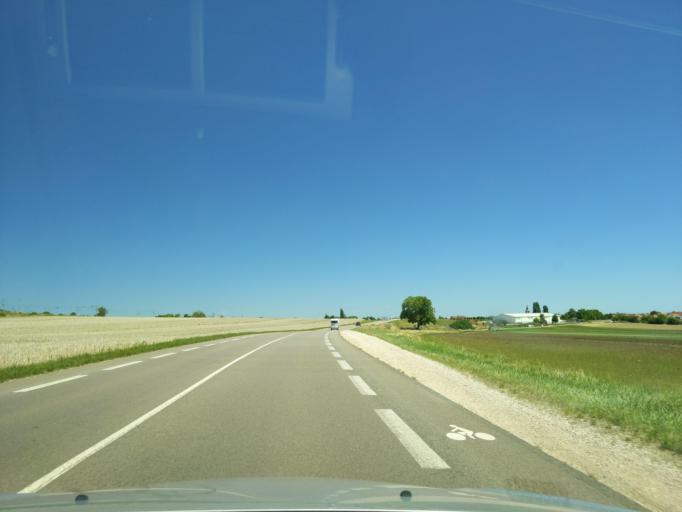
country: FR
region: Bourgogne
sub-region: Departement de la Cote-d'Or
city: Ruffey-les-Echirey
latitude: 47.3627
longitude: 5.0693
